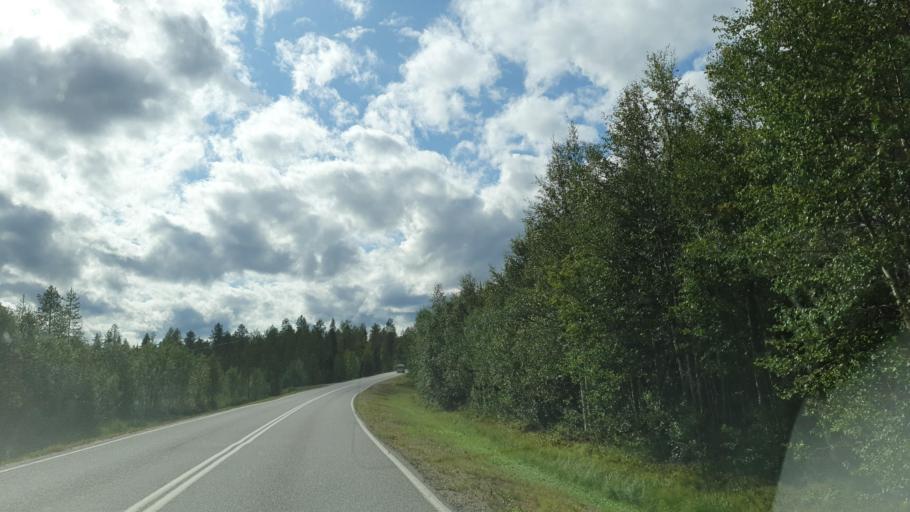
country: FI
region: Lapland
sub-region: Tunturi-Lappi
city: Muonio
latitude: 67.8758
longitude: 24.2041
